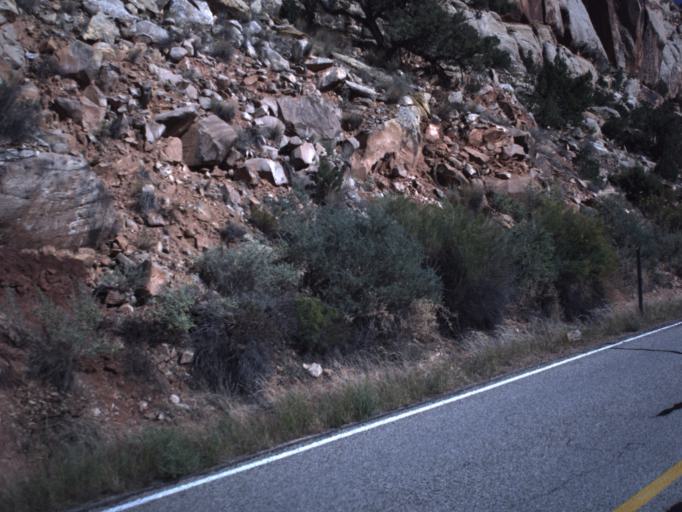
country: US
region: Utah
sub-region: San Juan County
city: Monticello
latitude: 38.0096
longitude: -109.5377
